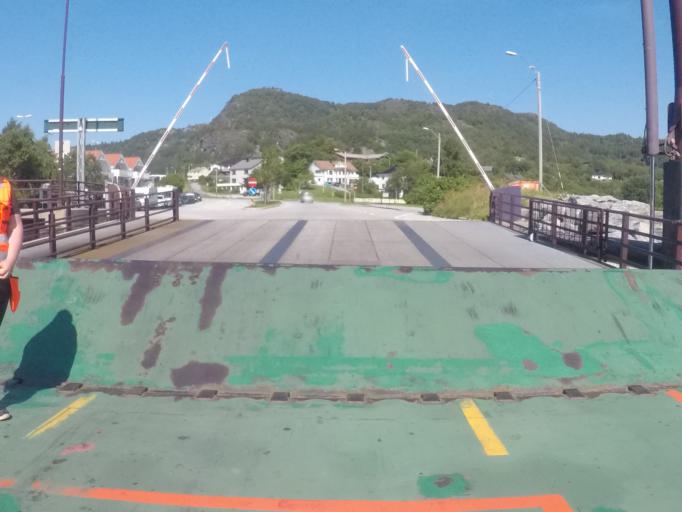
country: NO
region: More og Romsdal
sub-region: Sula
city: Langevag
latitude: 62.4136
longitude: 6.3275
